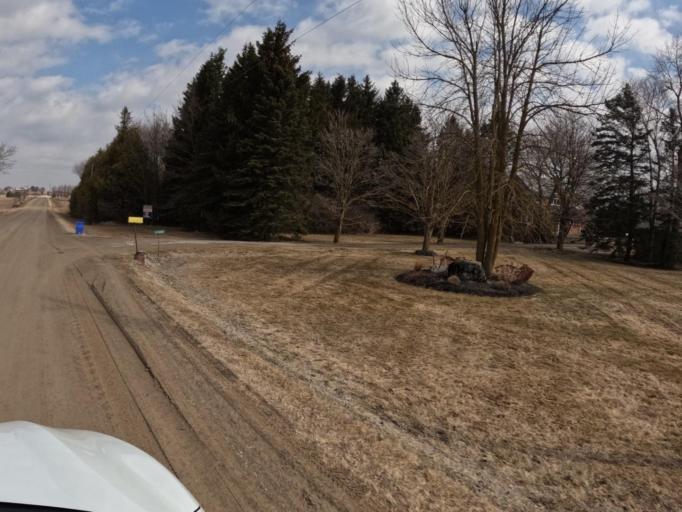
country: CA
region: Ontario
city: Orangeville
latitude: 43.9200
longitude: -80.2393
